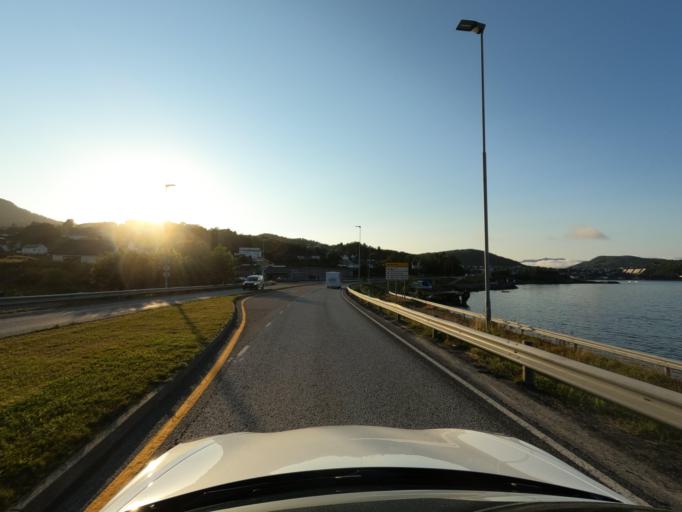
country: NO
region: Troms
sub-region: Harstad
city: Harstad
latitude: 68.7619
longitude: 16.5620
